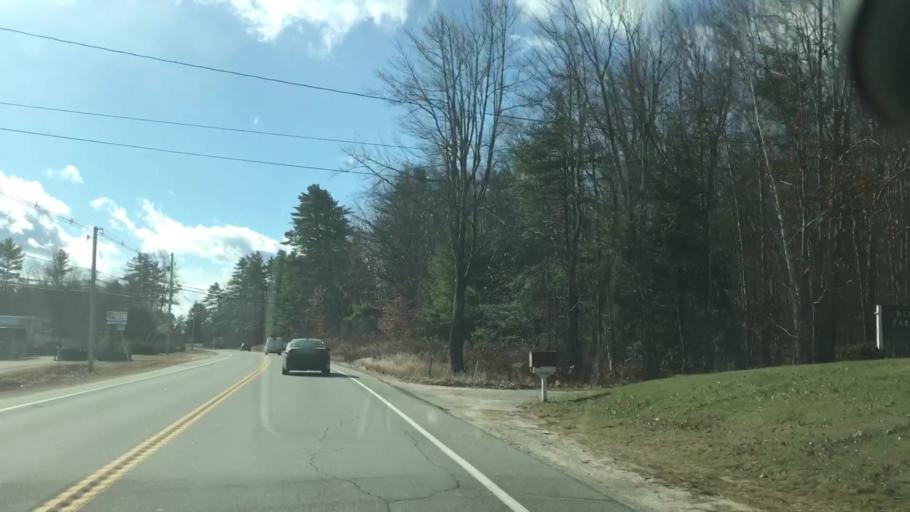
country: US
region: New Hampshire
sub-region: Carroll County
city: Wolfeboro
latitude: 43.6163
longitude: -71.1748
